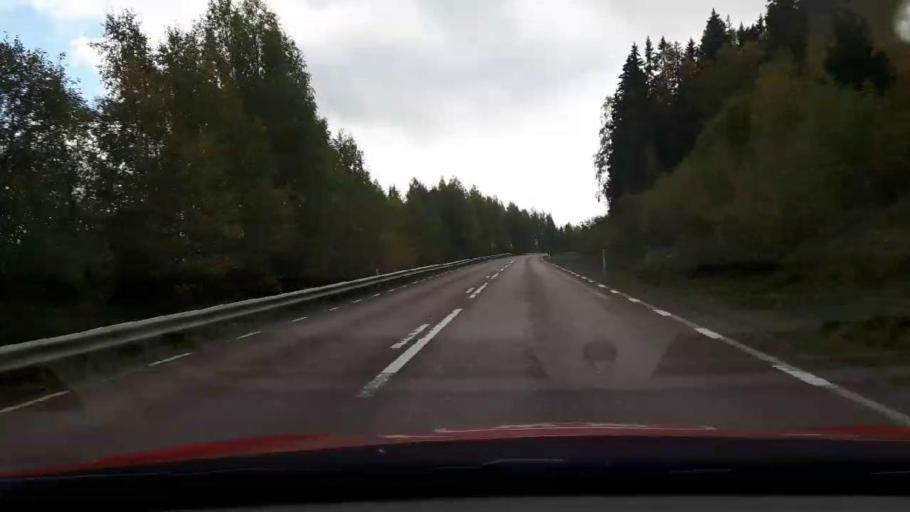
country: SE
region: Gaevleborg
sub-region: Bollnas Kommun
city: Arbra
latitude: 61.5574
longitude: 16.3449
